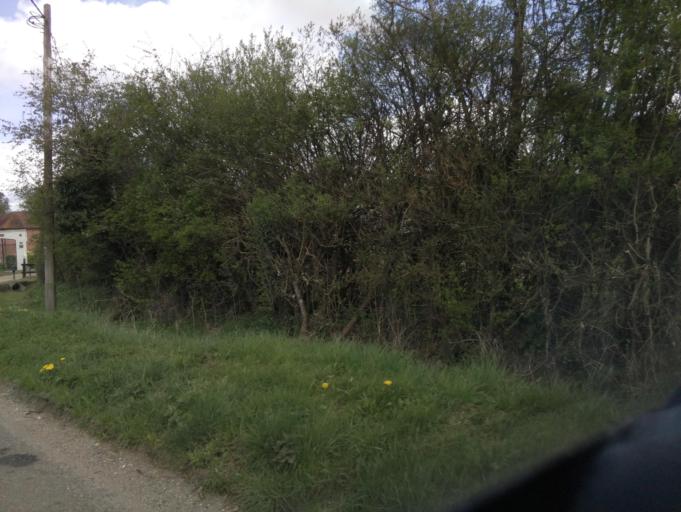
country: GB
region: England
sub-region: Hampshire
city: Andover
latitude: 51.2825
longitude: -1.4464
